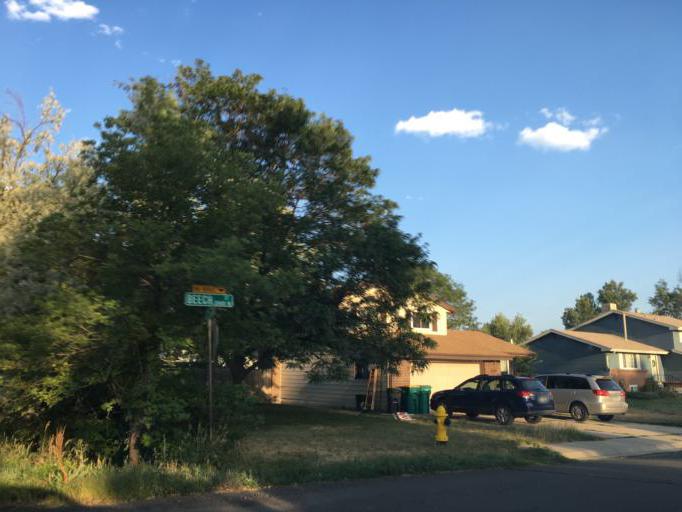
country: US
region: Colorado
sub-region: Jefferson County
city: Applewood
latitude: 39.7909
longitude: -105.1498
